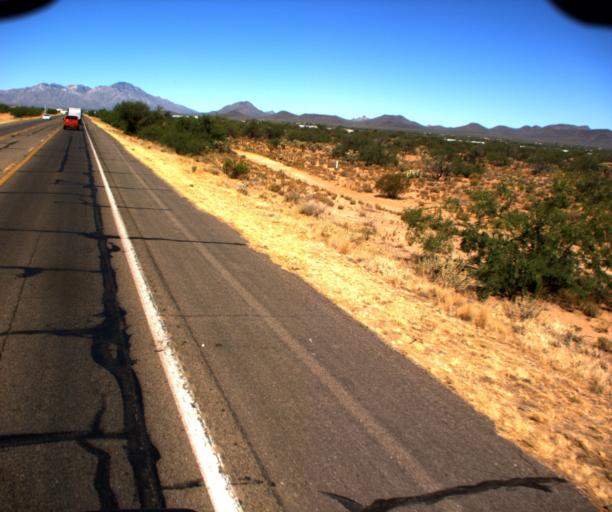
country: US
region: Arizona
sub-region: Pima County
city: Three Points
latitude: 32.0822
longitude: -111.2996
